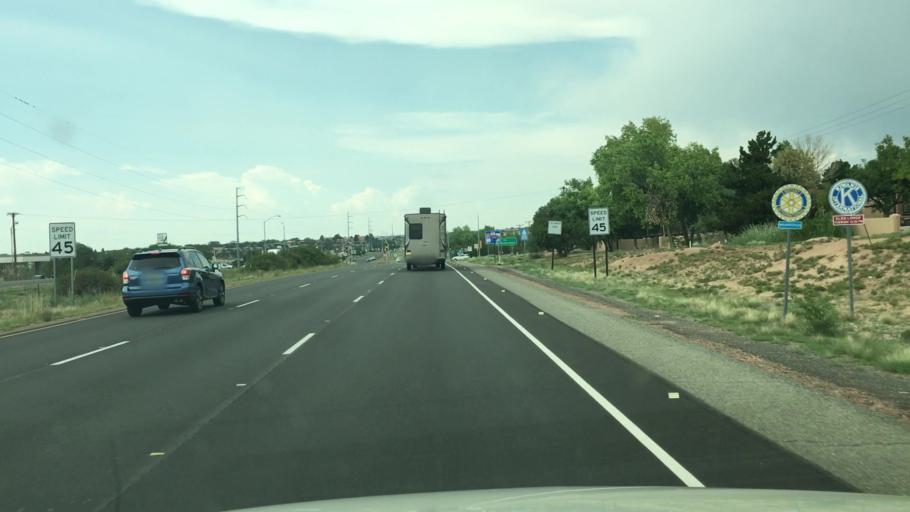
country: US
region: New Mexico
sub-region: Santa Fe County
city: Santa Fe
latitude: 35.6401
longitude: -105.9562
